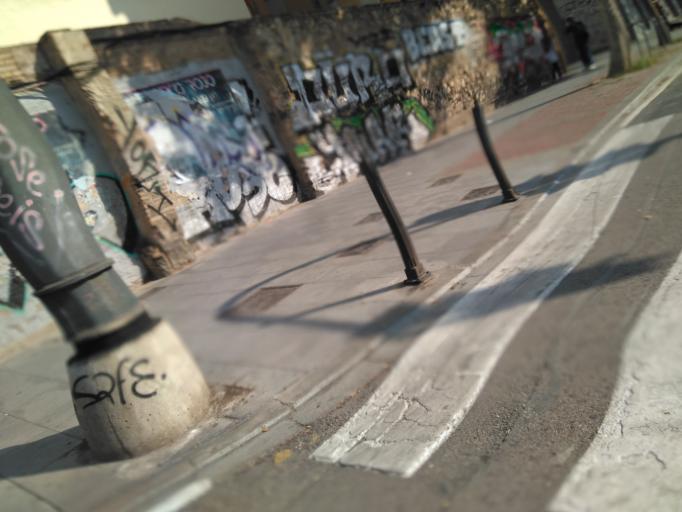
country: ES
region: Valencia
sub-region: Provincia de Valencia
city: Tavernes Blanques
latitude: 39.4848
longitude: -0.3709
